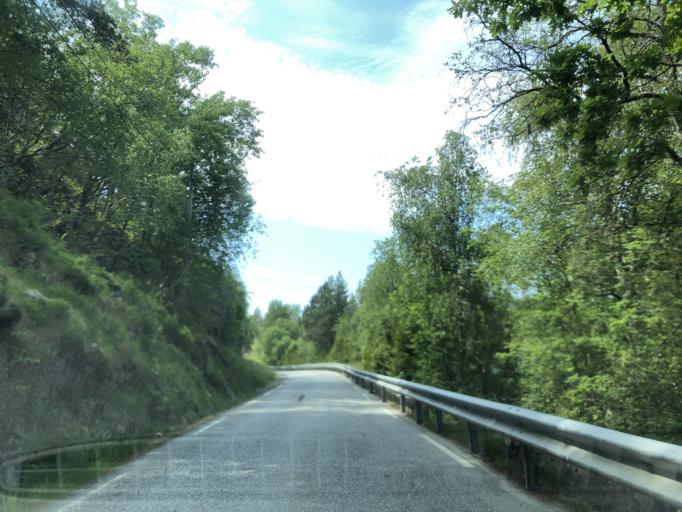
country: NO
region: Hordaland
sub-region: Jondal
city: Jondal
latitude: 60.3377
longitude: 6.3571
